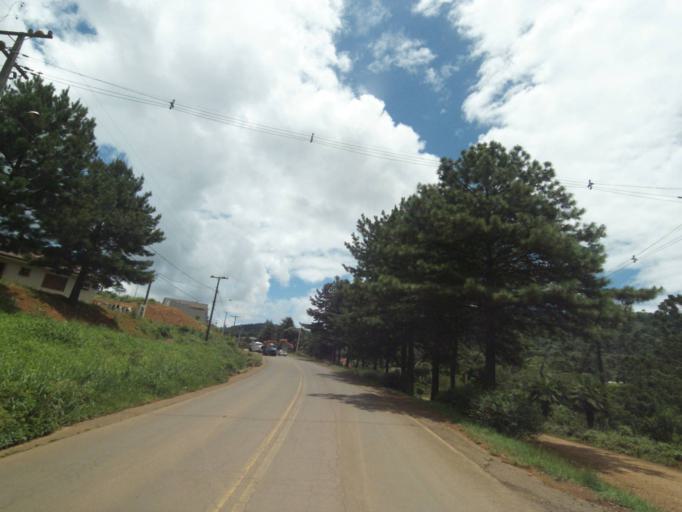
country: BR
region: Parana
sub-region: Pinhao
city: Pinhao
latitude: -26.1564
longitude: -51.5651
